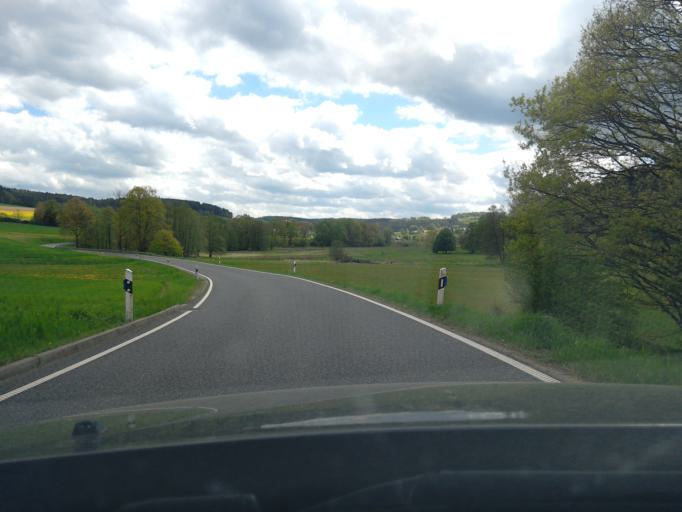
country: DE
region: Hesse
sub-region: Regierungsbezirk Darmstadt
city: Steinau an der Strasse
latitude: 50.2196
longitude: 9.4866
